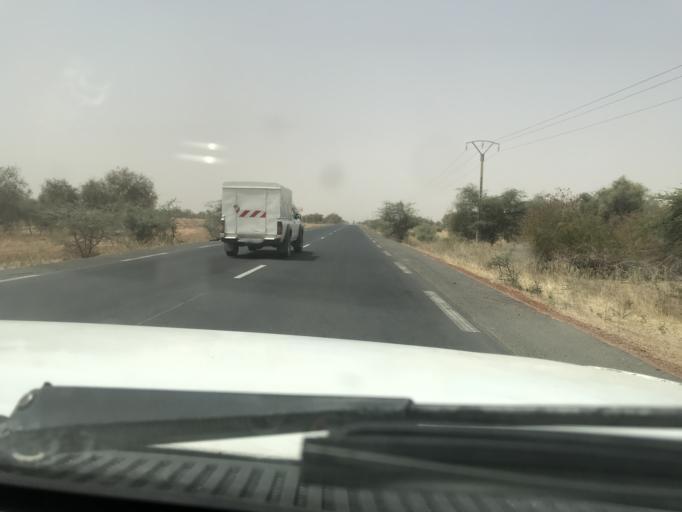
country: SN
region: Louga
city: Ndibene Dahra
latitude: 15.3432
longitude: -15.3833
